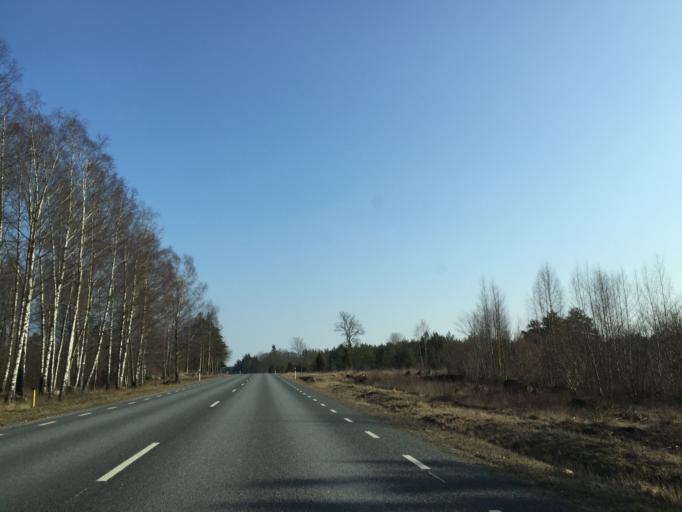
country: EE
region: Saare
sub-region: Orissaare vald
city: Orissaare
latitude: 58.5945
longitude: 23.3285
